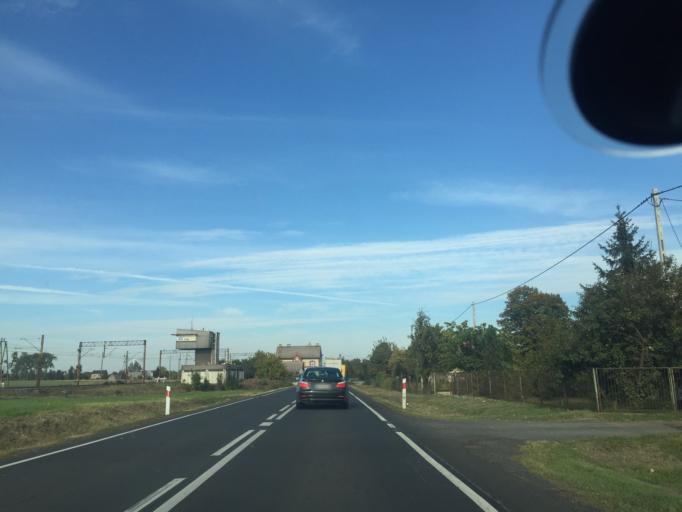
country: PL
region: Kujawsko-Pomorskie
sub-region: Powiat mogilenski
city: Mogilno
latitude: 52.6070
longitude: 17.9008
